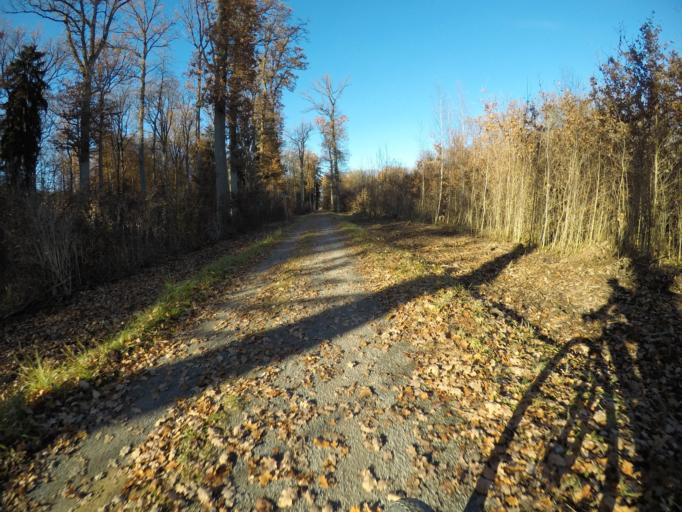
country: DE
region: Baden-Wuerttemberg
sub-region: Regierungsbezirk Stuttgart
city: Ehningen
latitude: 48.6784
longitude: 8.9595
